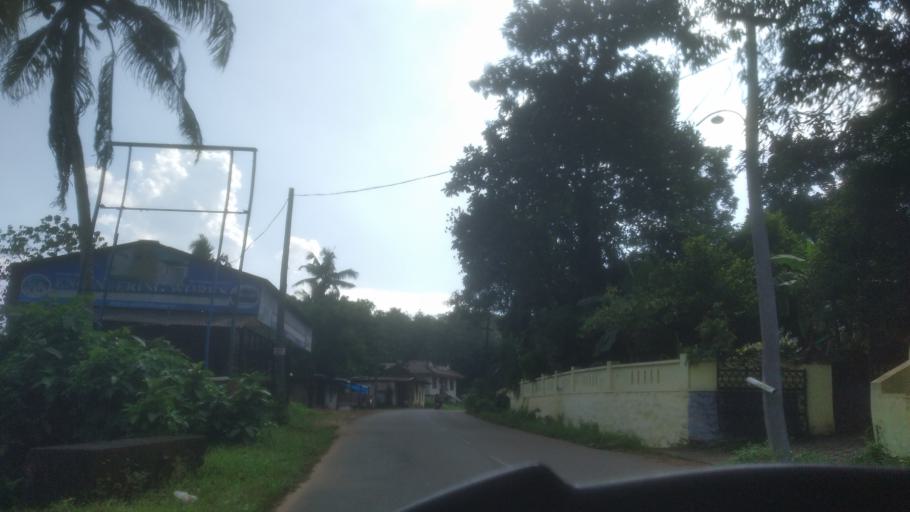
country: IN
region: Kerala
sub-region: Ernakulam
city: Kotamangalam
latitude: 9.9985
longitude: 76.6433
